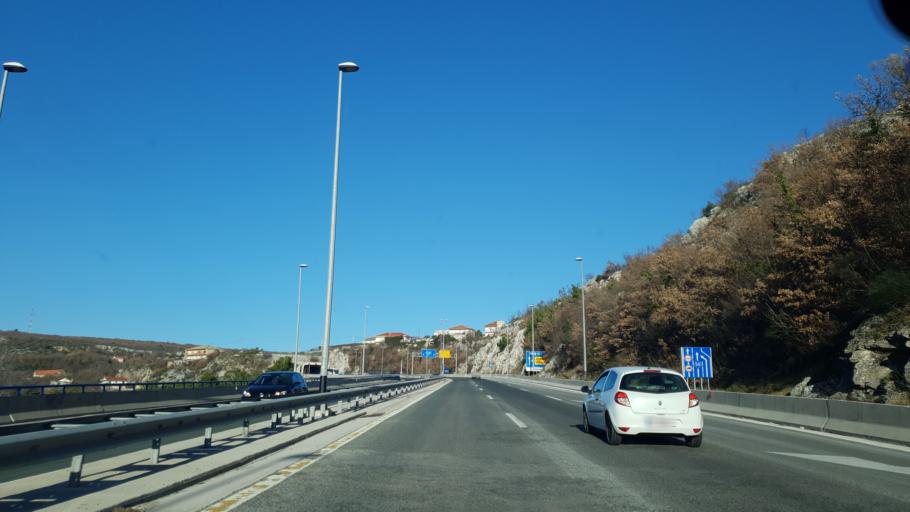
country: HR
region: Splitsko-Dalmatinska
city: Klis
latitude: 43.5680
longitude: 16.5322
